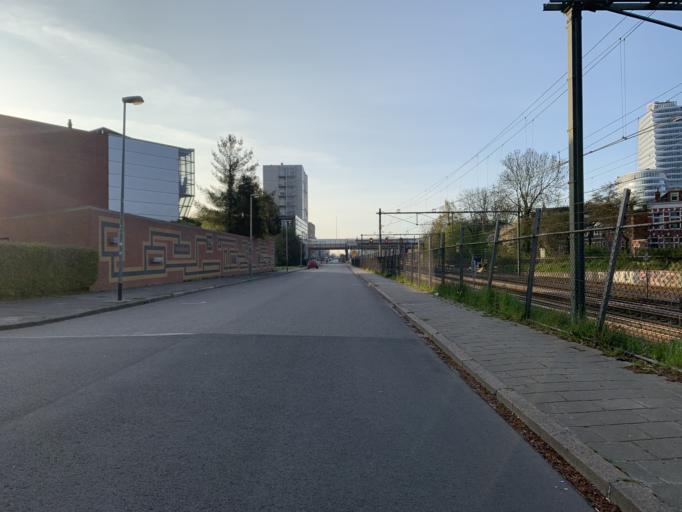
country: NL
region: Groningen
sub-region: Gemeente Groningen
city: Groningen
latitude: 53.2089
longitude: 6.5773
